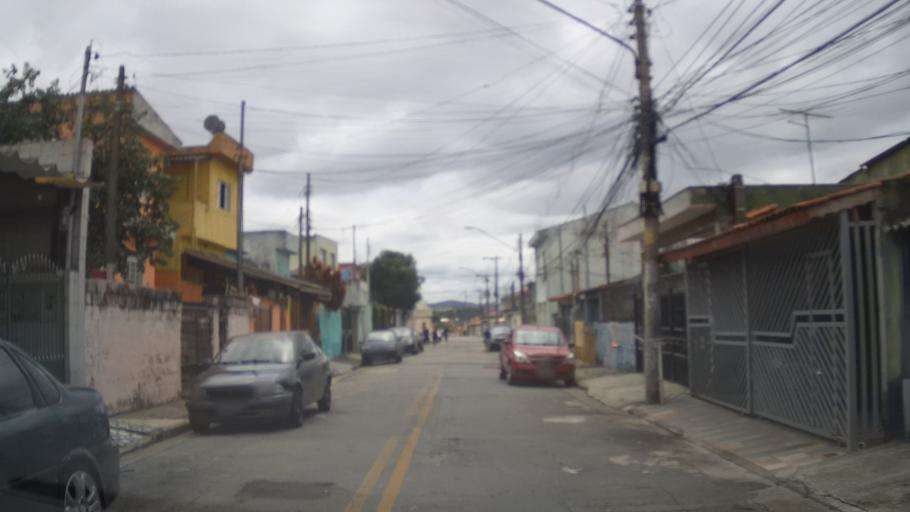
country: BR
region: Sao Paulo
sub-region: Guarulhos
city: Guarulhos
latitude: -23.4613
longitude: -46.5066
